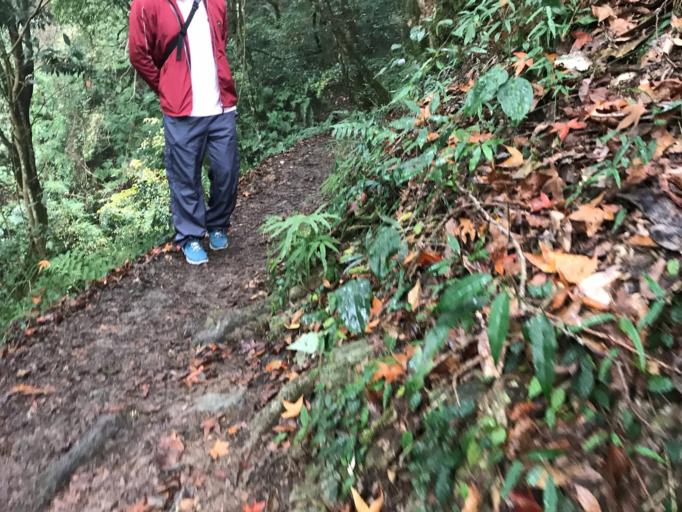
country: TW
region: Taiwan
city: Daxi
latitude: 24.5525
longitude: 121.2922
